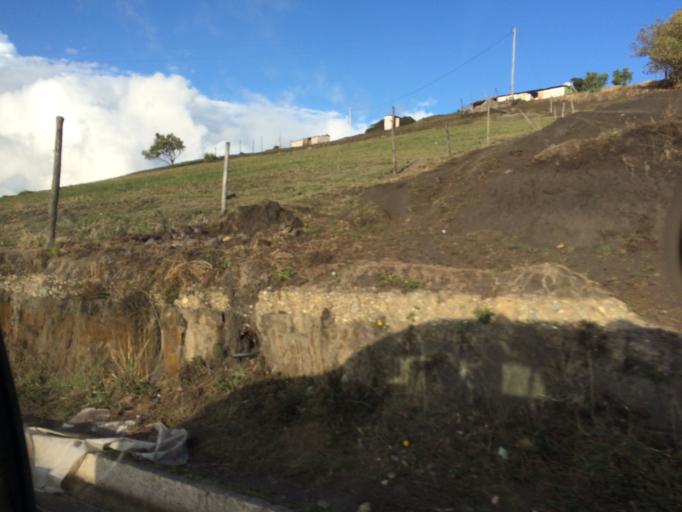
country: EC
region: Chimborazo
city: Alausi
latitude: -2.1380
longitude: -78.7190
